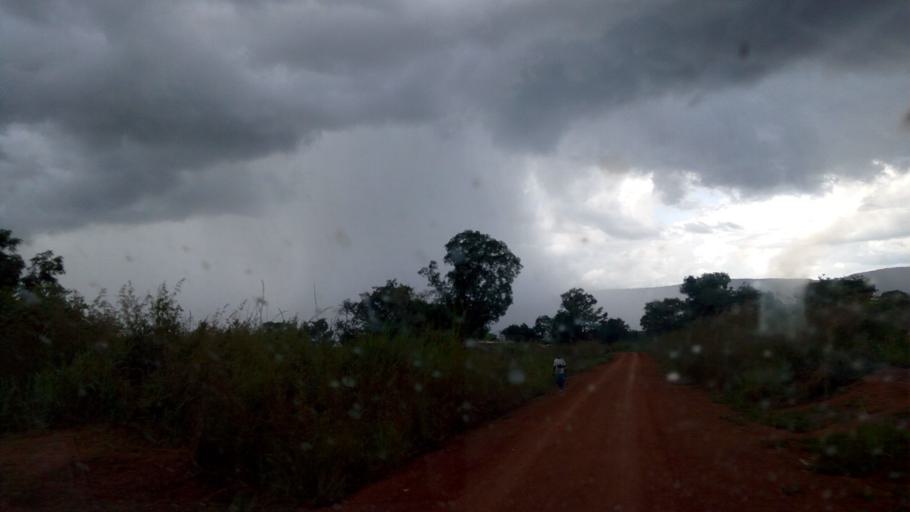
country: ZM
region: Northern
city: Kaputa
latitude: -8.0643
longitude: 29.1739
